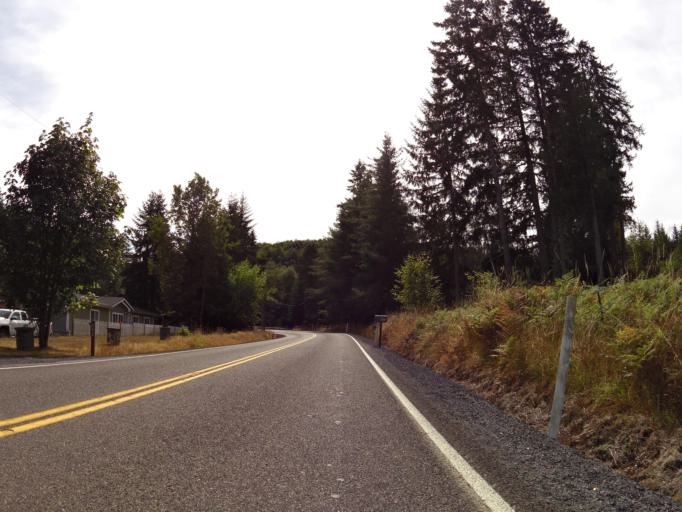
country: US
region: Washington
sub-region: Lewis County
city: Napavine
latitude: 46.5631
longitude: -122.9655
